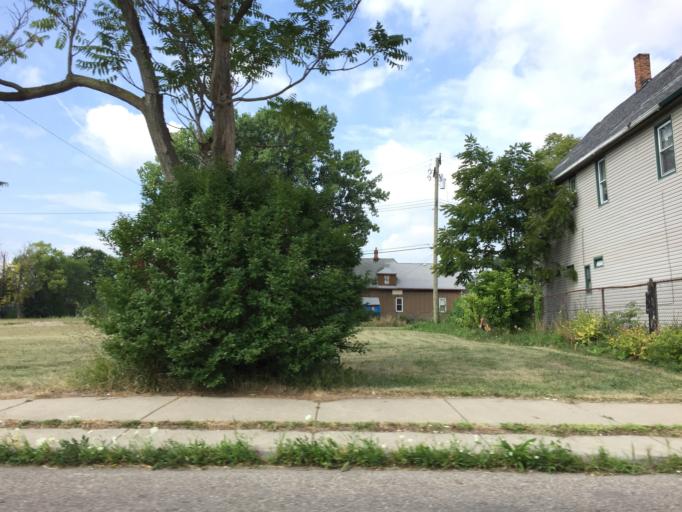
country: US
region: Michigan
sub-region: Wayne County
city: Detroit
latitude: 42.3604
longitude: -83.0374
